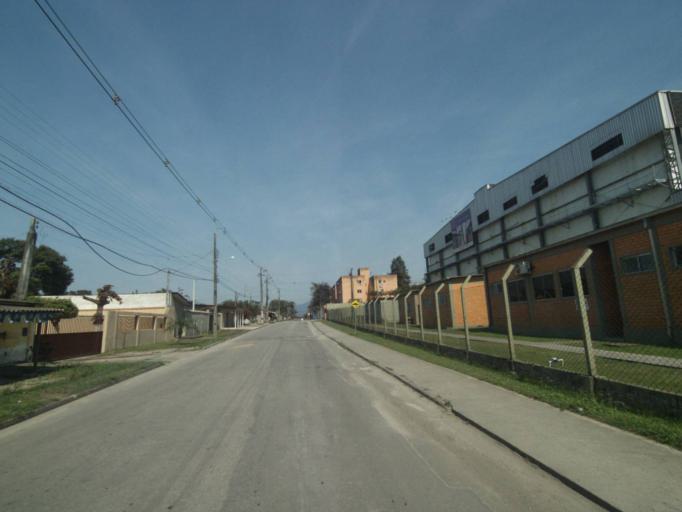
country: BR
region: Parana
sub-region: Paranagua
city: Paranagua
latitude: -25.5487
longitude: -48.5519
